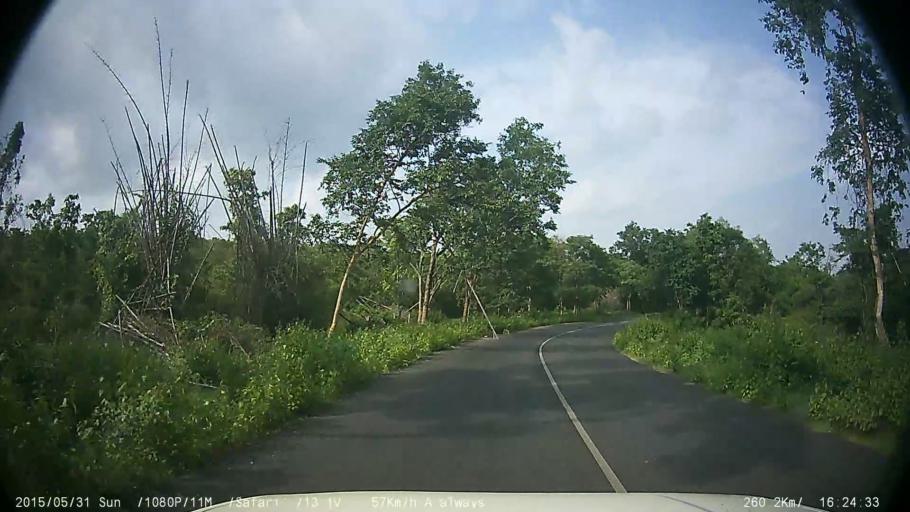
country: IN
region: Karnataka
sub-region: Chamrajnagar
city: Gundlupet
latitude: 11.7647
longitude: 76.5220
